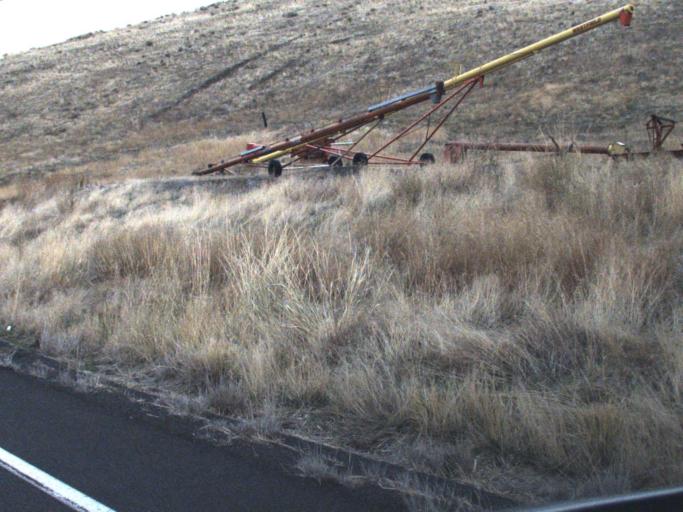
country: US
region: Washington
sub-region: Garfield County
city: Pomeroy
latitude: 46.4540
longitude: -117.4714
